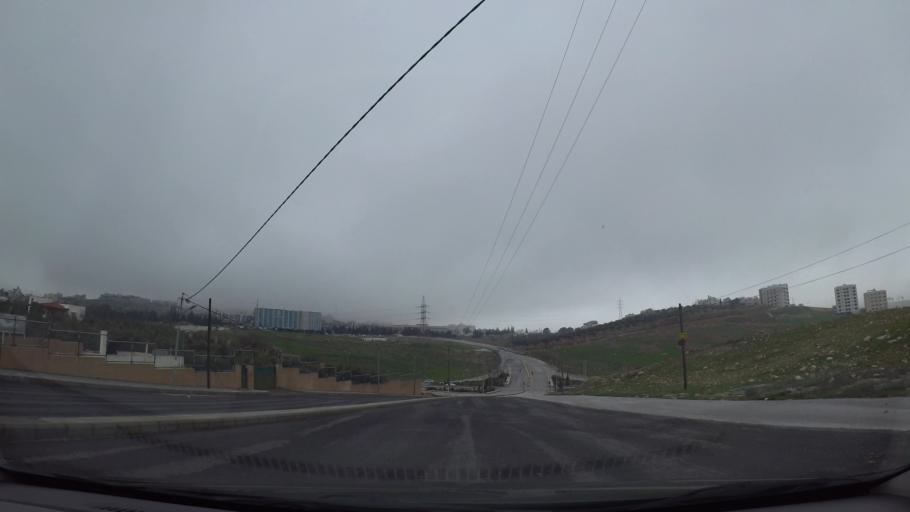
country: JO
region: Amman
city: Umm as Summaq
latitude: 31.9184
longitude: 35.8646
